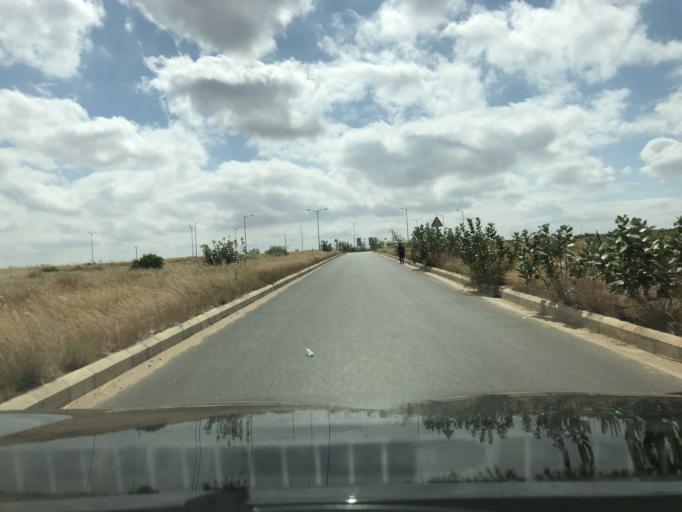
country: AO
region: Luanda
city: Luanda
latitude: -8.9653
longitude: 13.2438
